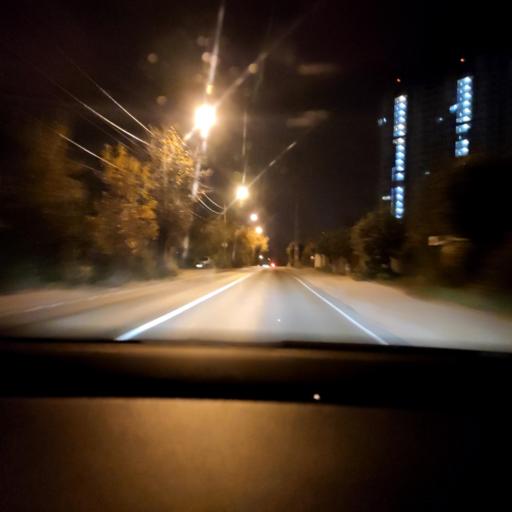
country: RU
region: Moskovskaya
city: Bolshevo
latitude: 55.9456
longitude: 37.8317
